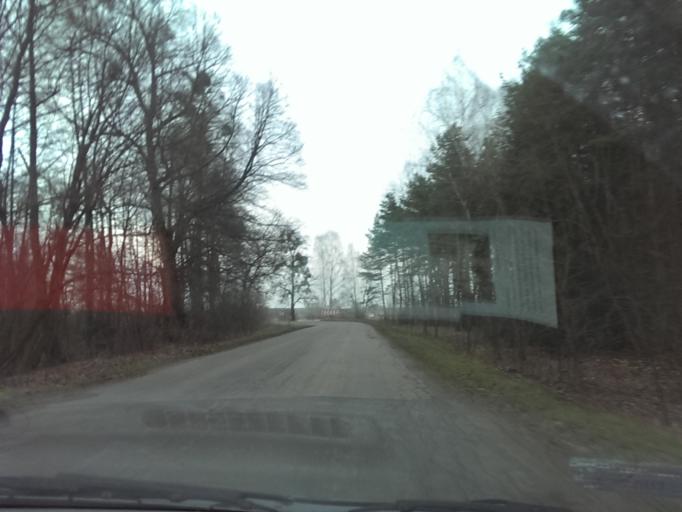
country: PL
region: Kujawsko-Pomorskie
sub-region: Powiat nakielski
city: Szubin
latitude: 53.0789
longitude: 17.7313
